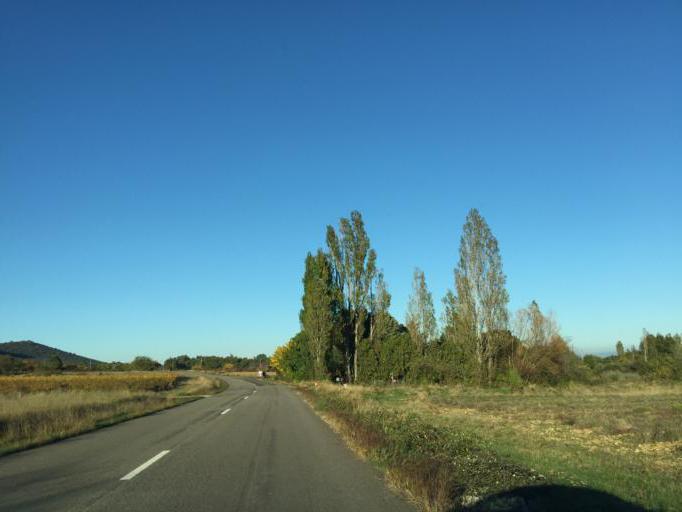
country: FR
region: Languedoc-Roussillon
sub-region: Departement du Gard
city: Saint-Julien-de-Peyrolas
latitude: 44.4028
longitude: 4.5120
